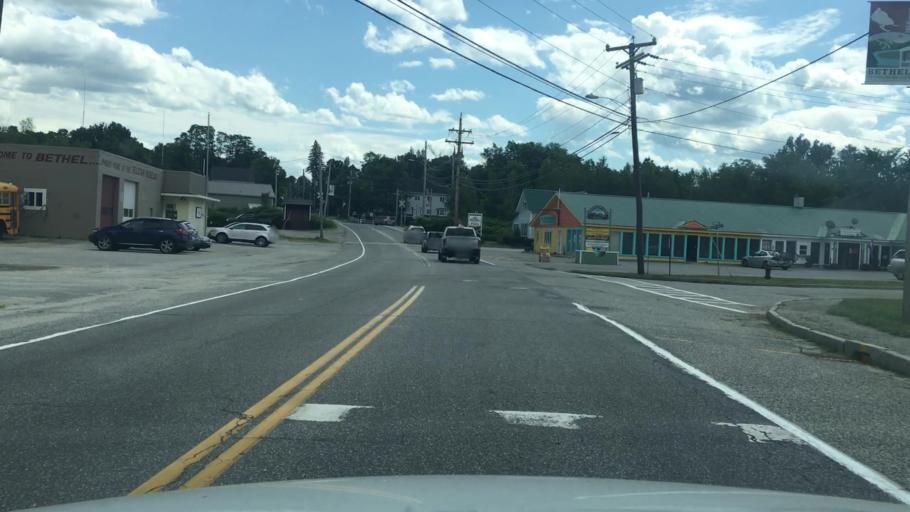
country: US
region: Maine
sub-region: Oxford County
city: Bethel
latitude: 44.4120
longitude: -70.7880
